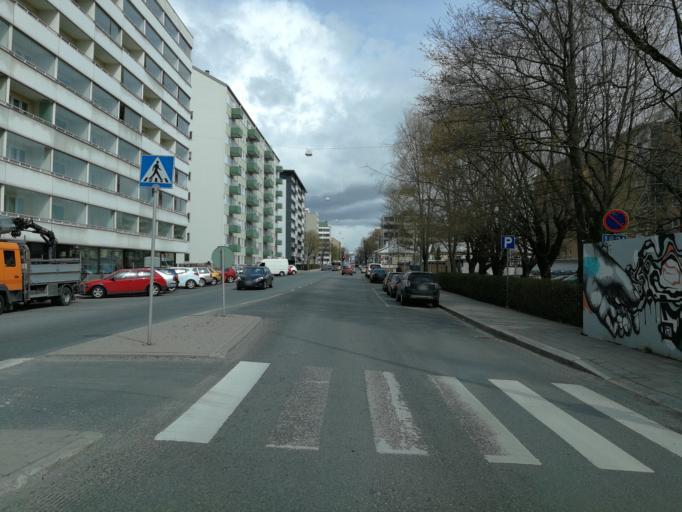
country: FI
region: Varsinais-Suomi
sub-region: Turku
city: Turku
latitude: 60.4418
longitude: 22.2695
